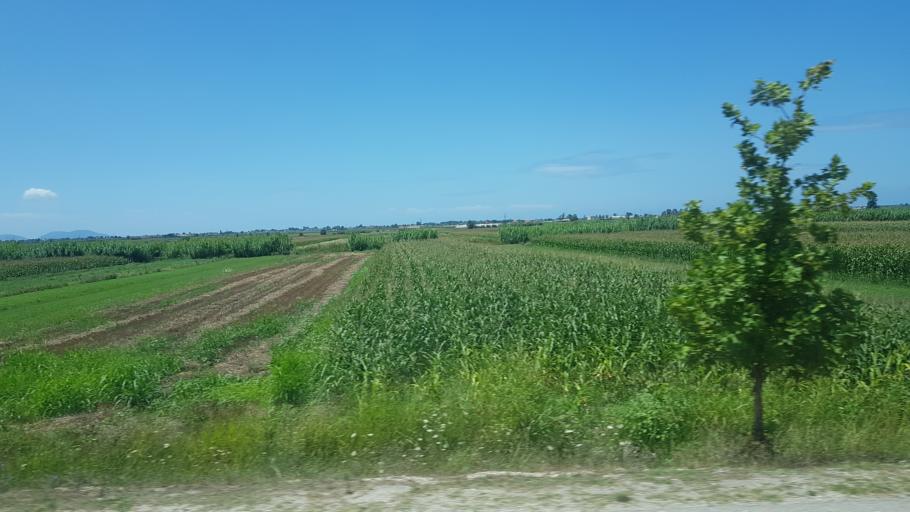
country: AL
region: Fier
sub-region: Rrethi i Fierit
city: Frakulla e Madhe
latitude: 40.6579
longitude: 19.4904
